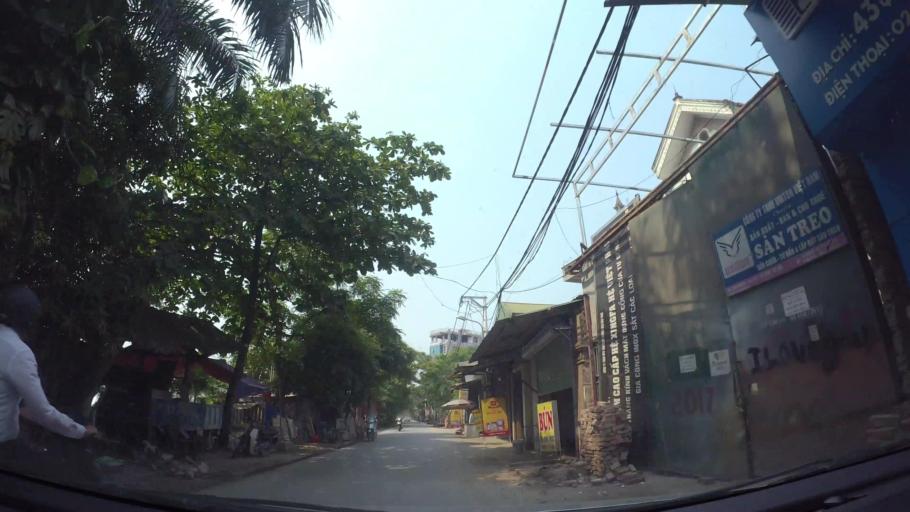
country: VN
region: Ha Noi
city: Cau Dien
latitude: 21.0041
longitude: 105.7590
